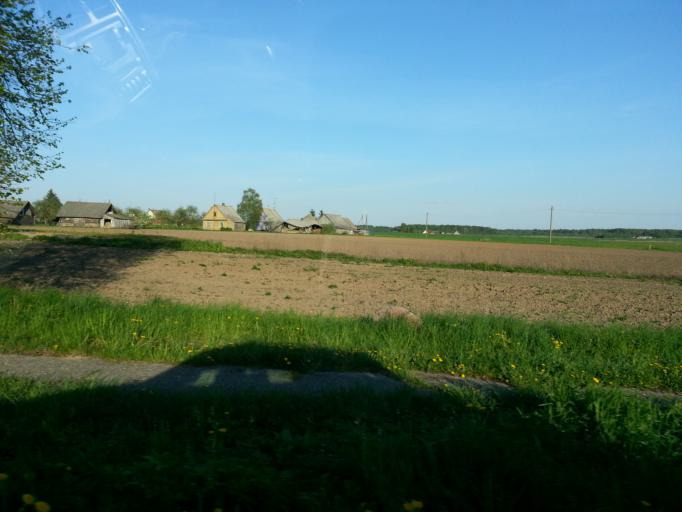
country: LT
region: Vilnius County
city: Ukmerge
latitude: 55.4268
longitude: 24.5894
